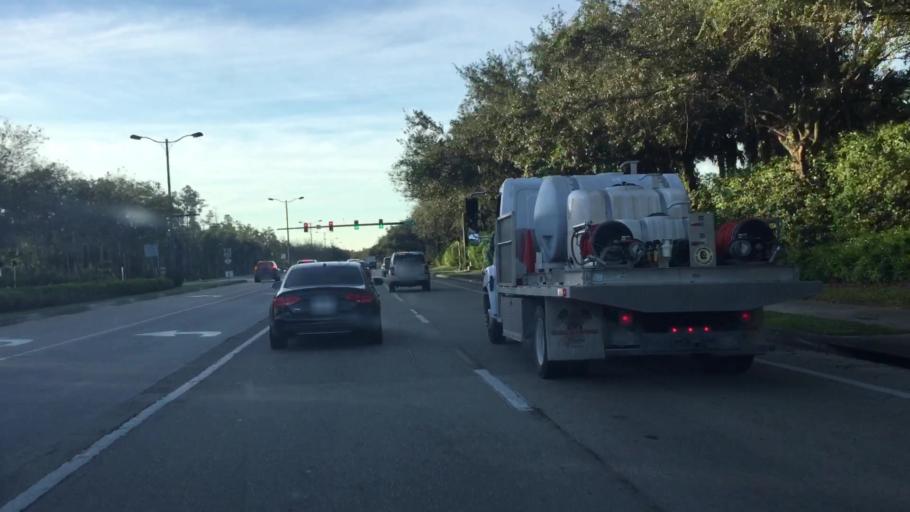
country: US
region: Florida
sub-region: Lee County
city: Three Oaks
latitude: 26.4711
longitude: -81.7864
